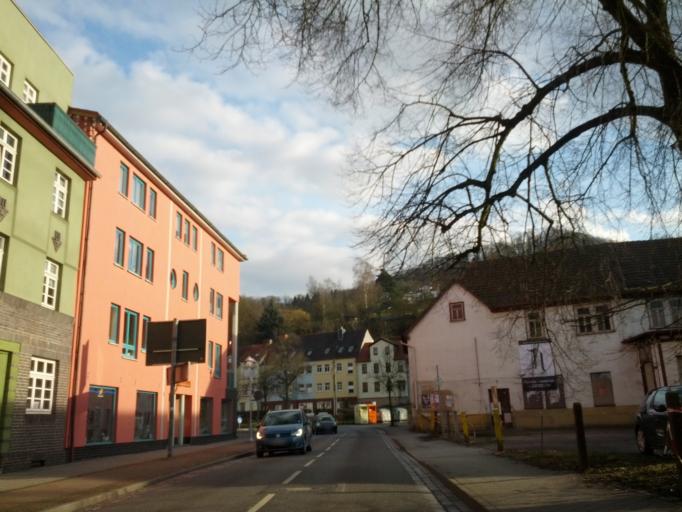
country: DE
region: Thuringia
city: Eisenach
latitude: 50.9775
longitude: 10.3051
